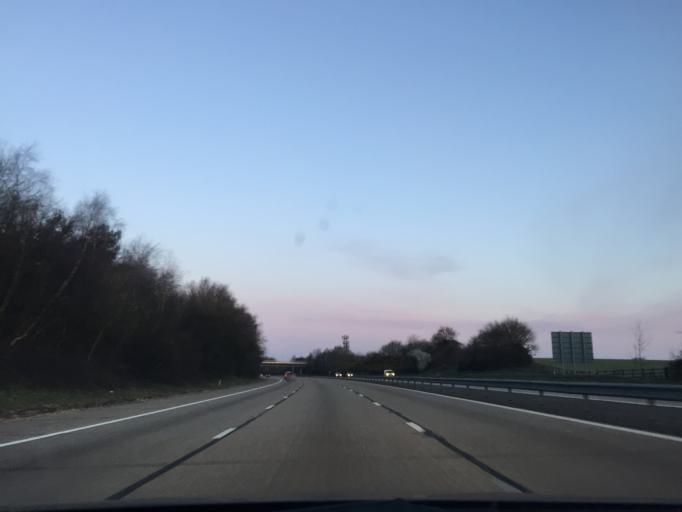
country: GB
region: England
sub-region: Hampshire
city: West End
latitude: 50.9335
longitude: -1.3259
